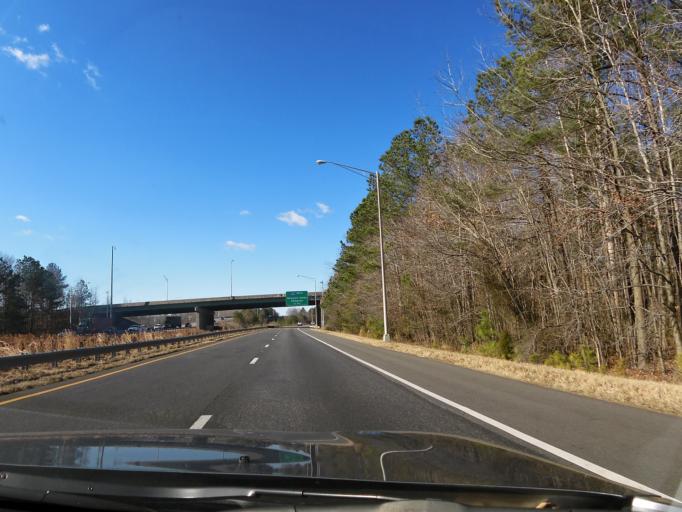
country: US
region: Virginia
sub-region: City of Portsmouth
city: Portsmouth Heights
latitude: 36.8678
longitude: -76.4205
